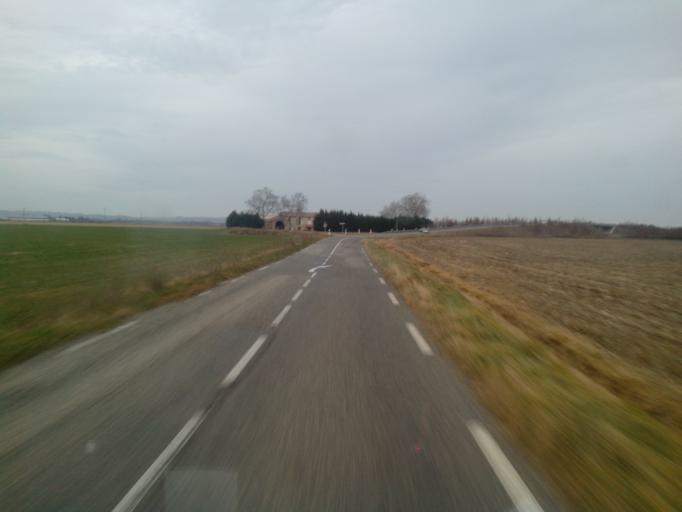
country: FR
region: Midi-Pyrenees
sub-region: Departement de l'Ariege
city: Mazeres
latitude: 43.2165
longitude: 1.6334
